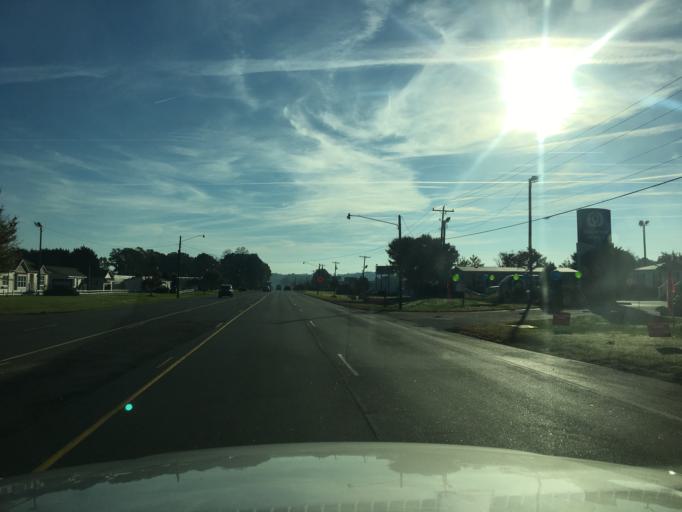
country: US
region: North Carolina
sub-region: Catawba County
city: Conover
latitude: 35.6967
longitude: -81.2587
